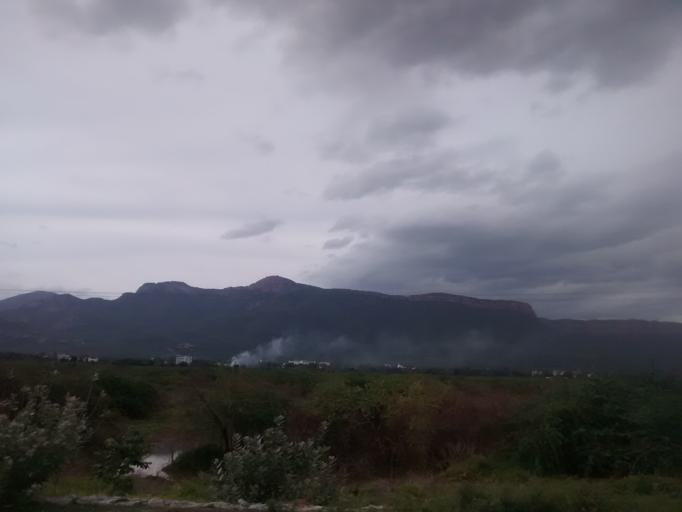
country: IN
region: Andhra Pradesh
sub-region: Chittoor
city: Narasingapuram
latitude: 13.6032
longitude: 79.3712
